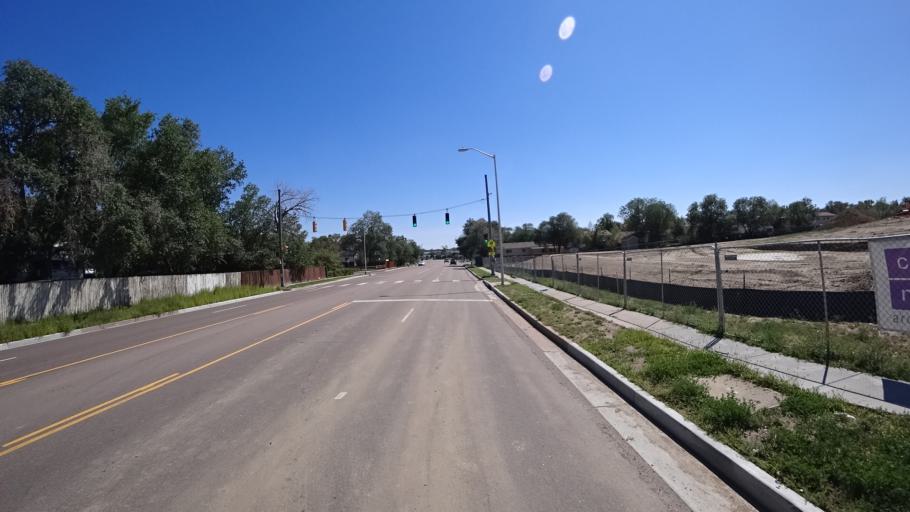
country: US
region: Colorado
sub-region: El Paso County
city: Stratmoor
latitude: 38.8080
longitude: -104.7643
